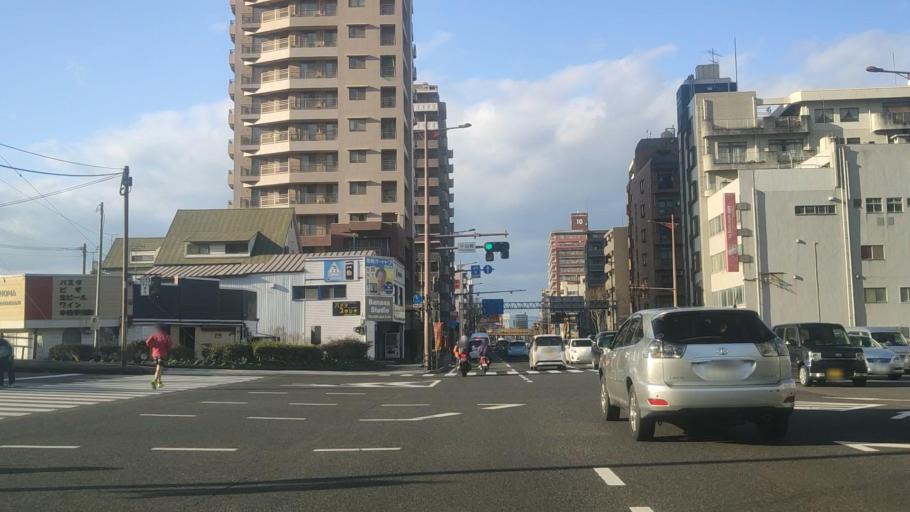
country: JP
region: Kagoshima
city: Kagoshima-shi
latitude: 31.5902
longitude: 130.5460
